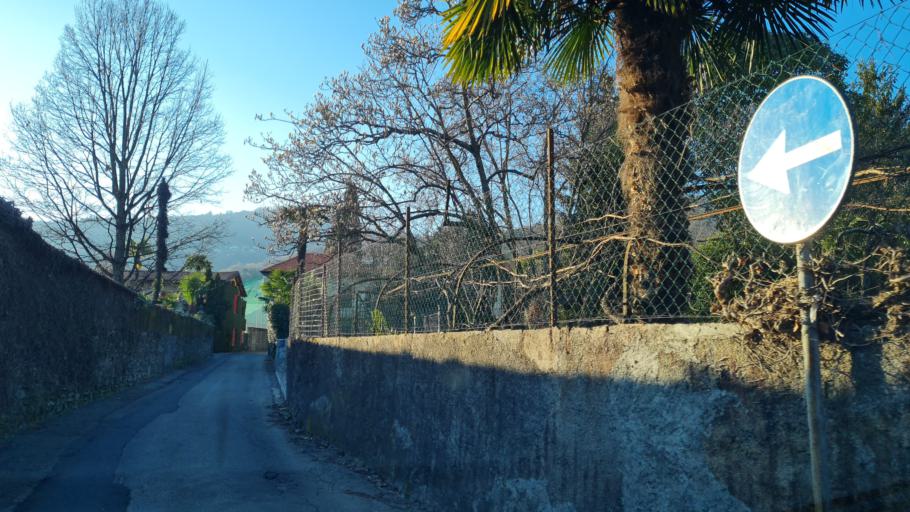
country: IT
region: Piedmont
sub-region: Provincia di Novara
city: Lesa
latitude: 45.8250
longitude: 8.5646
